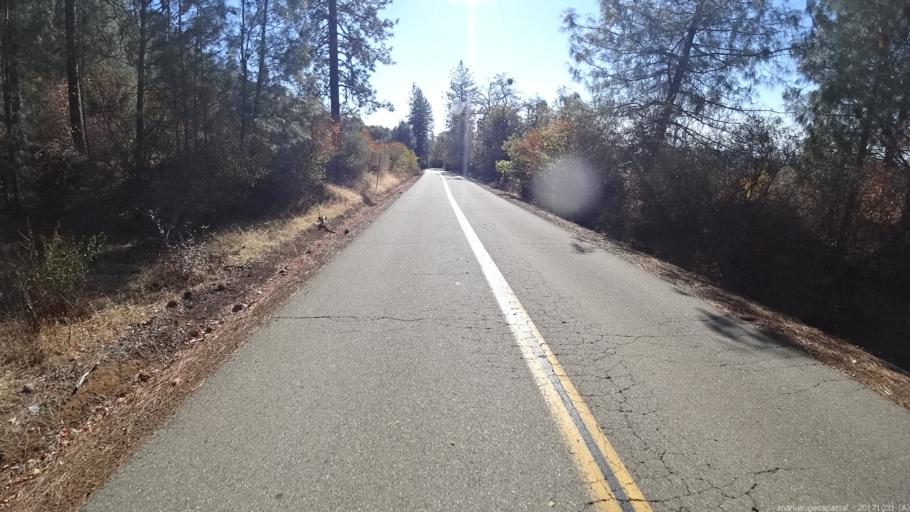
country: US
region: California
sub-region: Shasta County
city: Shingletown
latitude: 40.4600
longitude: -122.0037
